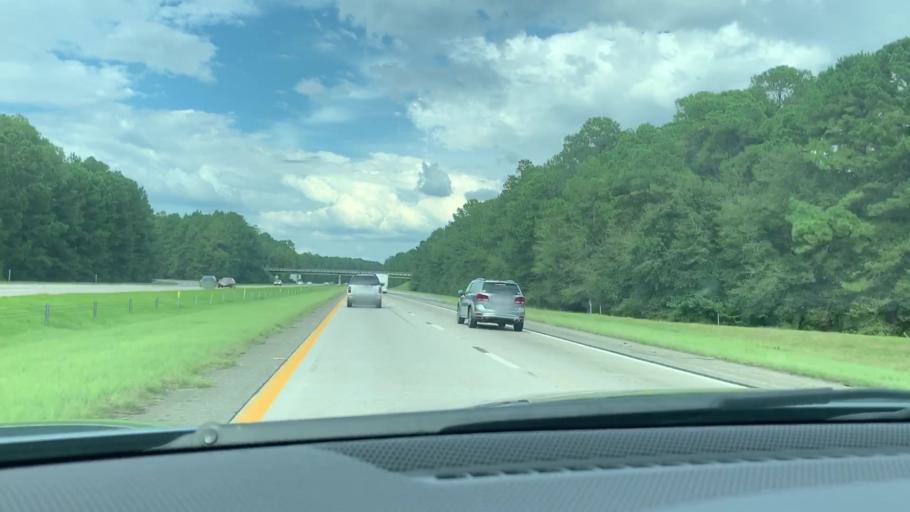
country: US
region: South Carolina
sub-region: Jasper County
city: Ridgeland
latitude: 32.4432
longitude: -80.9953
